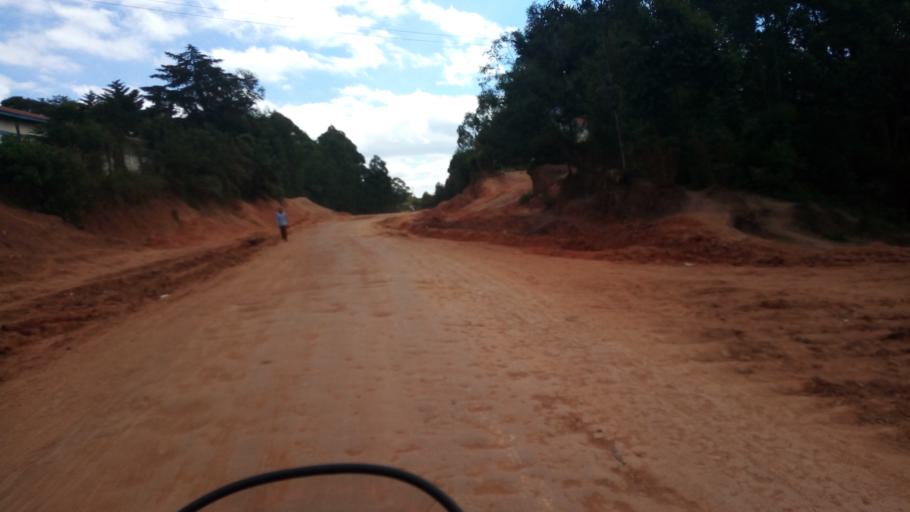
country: KE
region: Makueni
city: Wote
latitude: -1.6578
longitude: 37.4519
